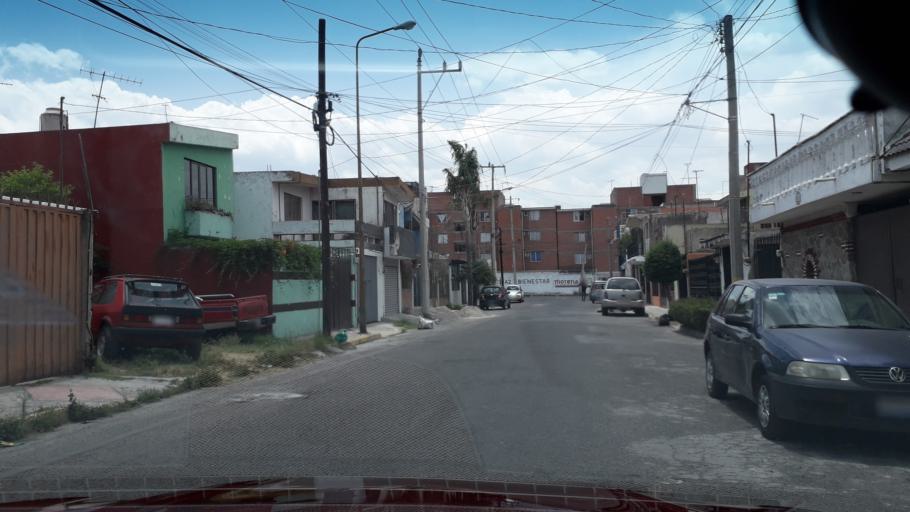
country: MX
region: Puebla
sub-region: Puebla
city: El Capulo (La Quebradora)
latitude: 18.9950
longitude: -98.2416
